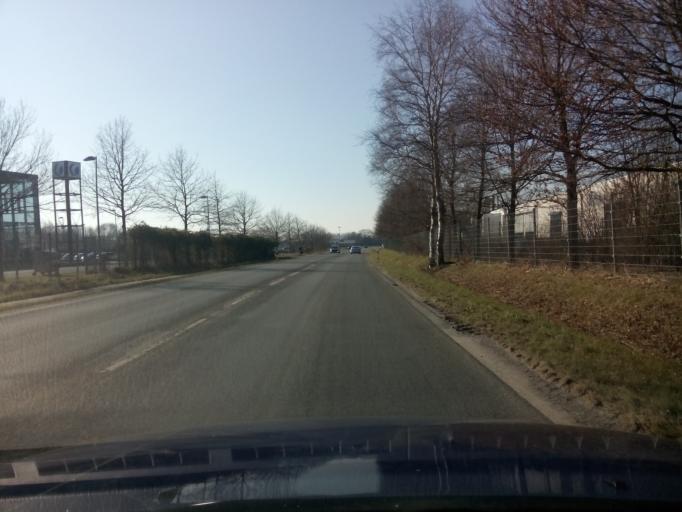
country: DE
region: Lower Saxony
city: Ritterhude
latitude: 53.2284
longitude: 8.7015
